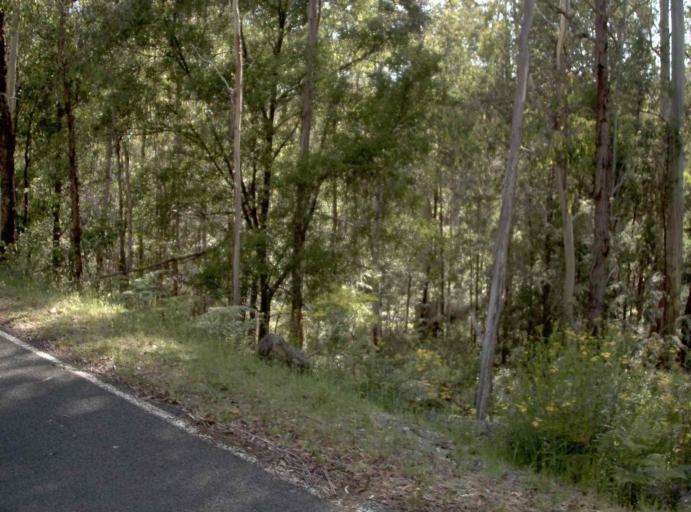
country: AU
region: New South Wales
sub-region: Bombala
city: Bombala
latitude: -37.3600
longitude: 148.6837
